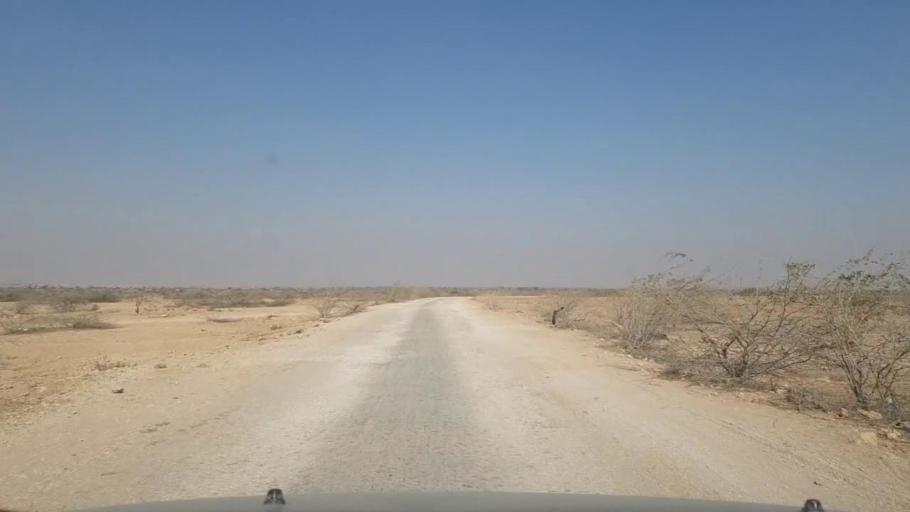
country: PK
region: Sindh
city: Thatta
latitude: 24.9287
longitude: 67.9388
